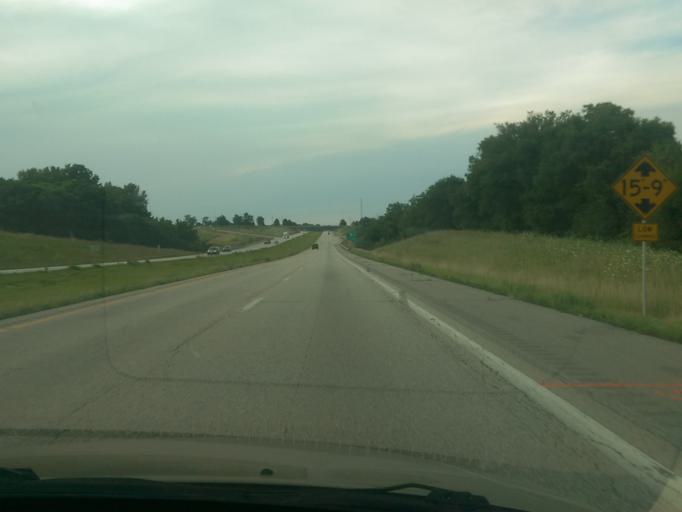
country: US
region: Missouri
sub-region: Andrew County
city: Country Club Village
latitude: 39.8076
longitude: -94.8011
